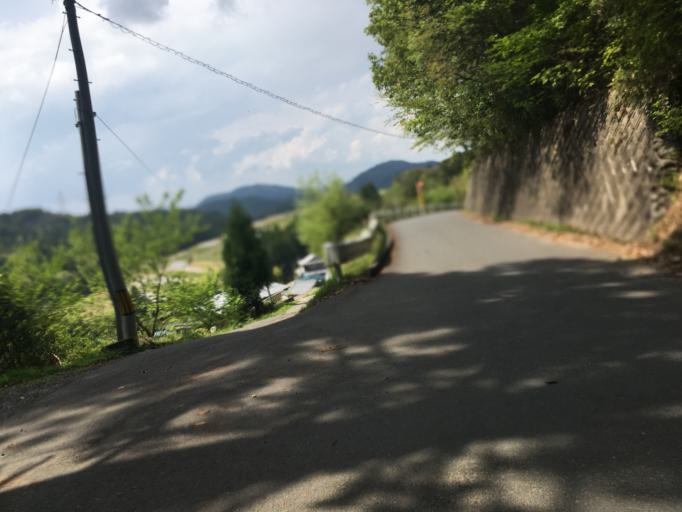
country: JP
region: Kyoto
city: Kameoka
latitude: 35.0707
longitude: 135.6111
